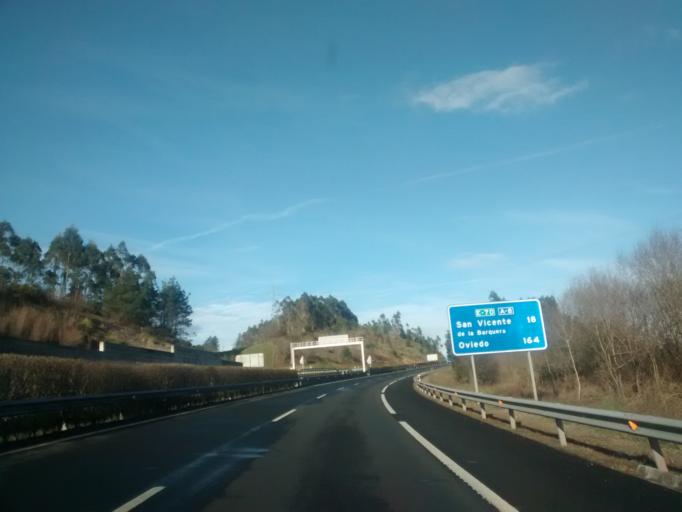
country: ES
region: Cantabria
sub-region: Provincia de Cantabria
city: Cabezon de la Sal
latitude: 43.3173
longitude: -4.2642
